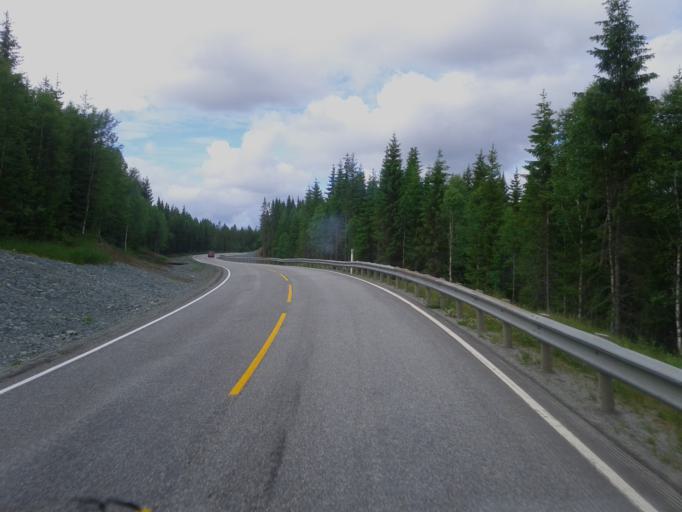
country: NO
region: Nord-Trondelag
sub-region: Hoylandet
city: Hoylandet
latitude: 64.6640
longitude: 12.6661
